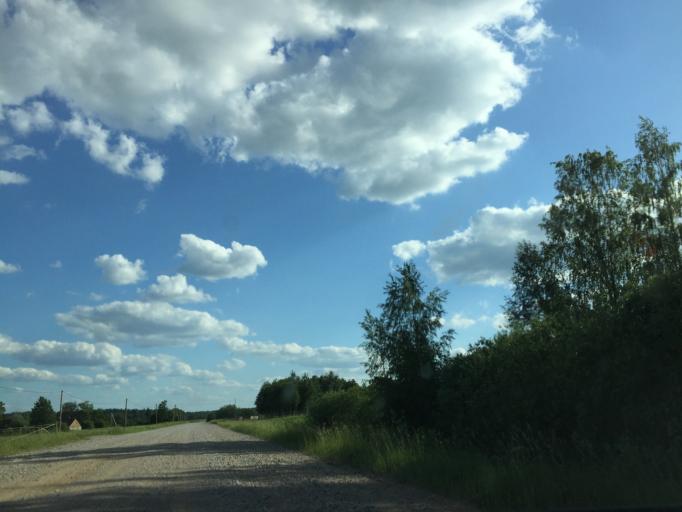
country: LV
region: Kandava
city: Kandava
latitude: 56.9007
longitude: 22.7913
